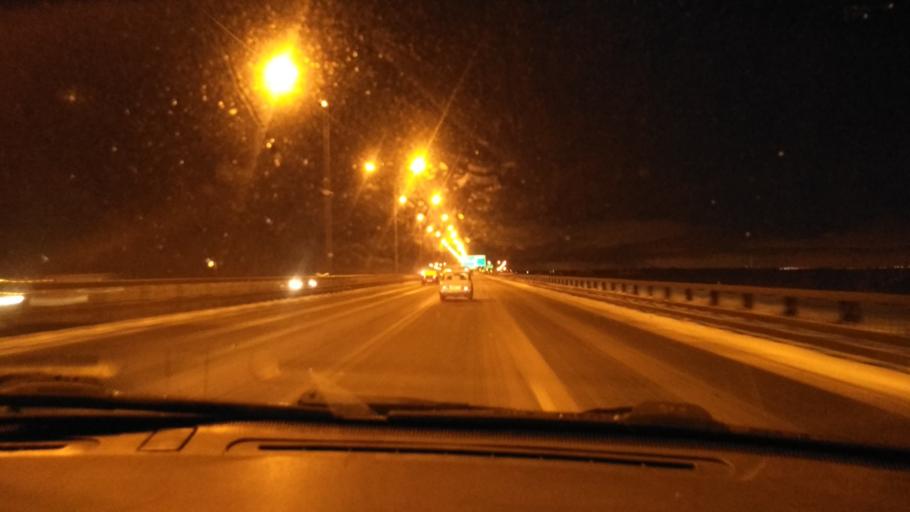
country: RU
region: St.-Petersburg
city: Kronshtadt
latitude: 60.0234
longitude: 29.8058
